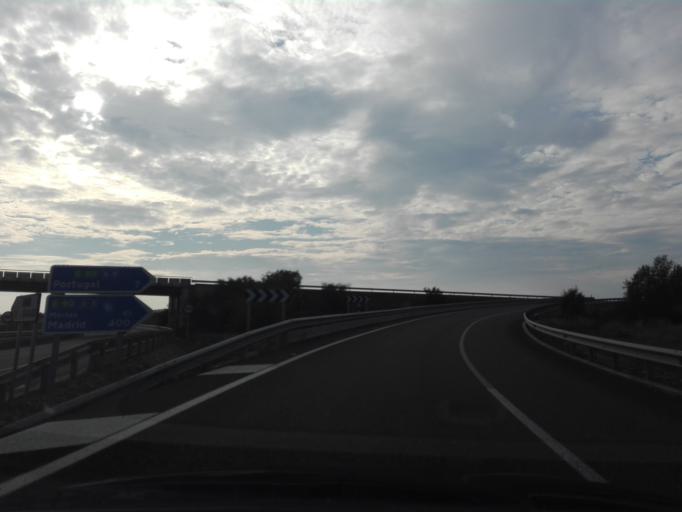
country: ES
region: Extremadura
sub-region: Provincia de Badajoz
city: Badajoz
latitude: 38.9172
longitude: -6.9611
